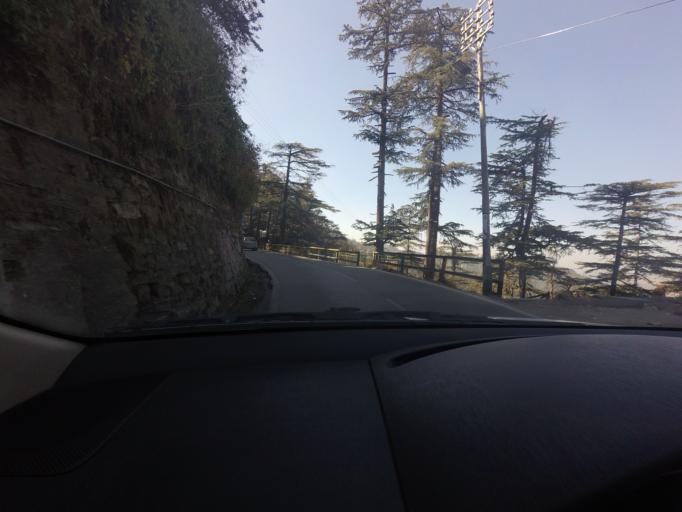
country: IN
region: Himachal Pradesh
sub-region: Shimla
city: Shimla
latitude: 31.1061
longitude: 77.1649
